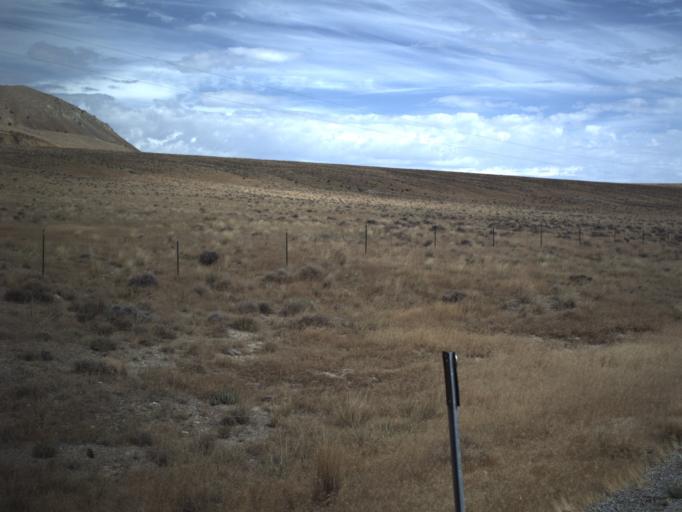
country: US
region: Utah
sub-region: Tooele County
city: Wendover
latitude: 41.4520
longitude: -113.6674
